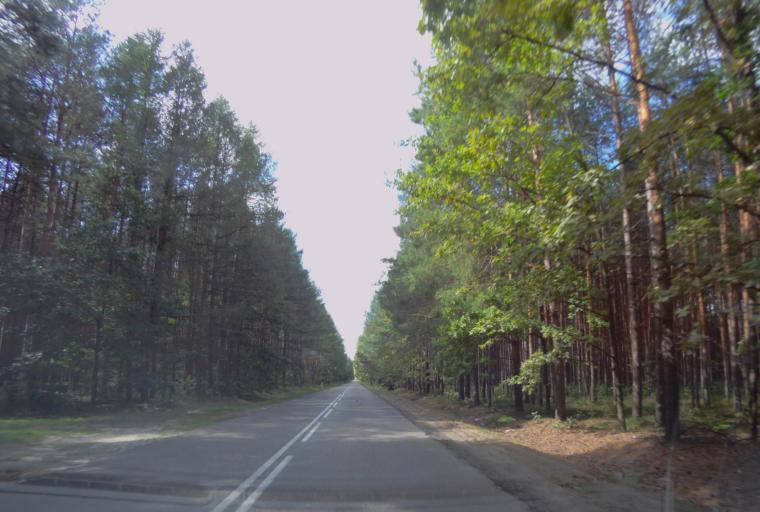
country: PL
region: Subcarpathian Voivodeship
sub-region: Powiat stalowowolski
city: Bojanow
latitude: 50.3982
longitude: 22.0255
